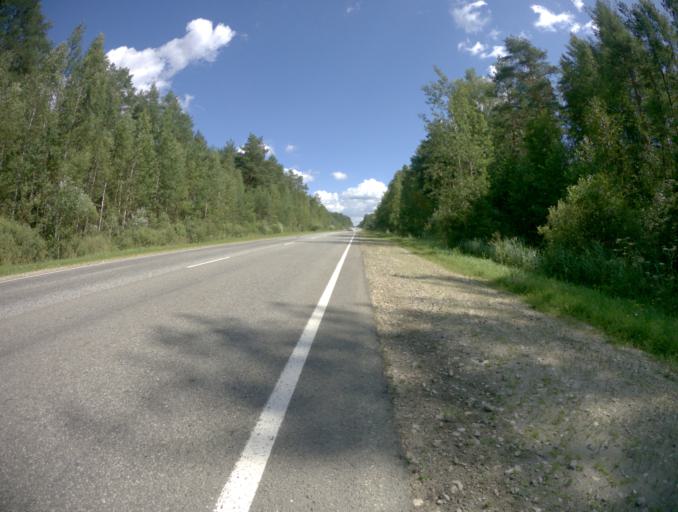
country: RU
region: Vladimir
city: Sudogda
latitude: 55.9714
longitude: 40.8135
